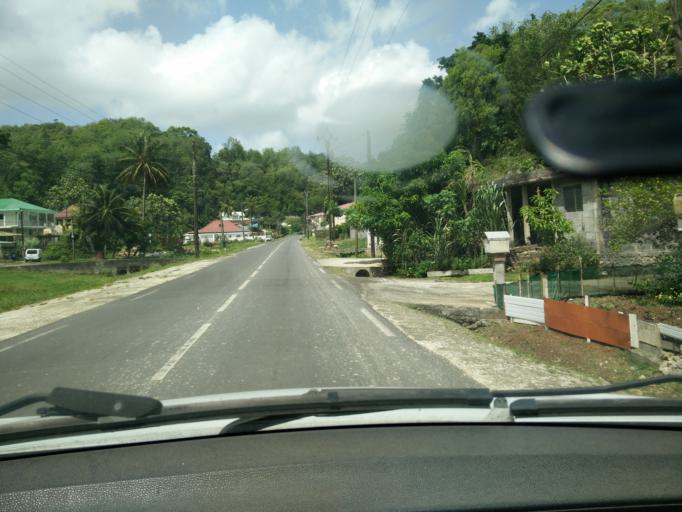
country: GP
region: Guadeloupe
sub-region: Guadeloupe
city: Les Abymes
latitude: 16.2902
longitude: -61.4661
